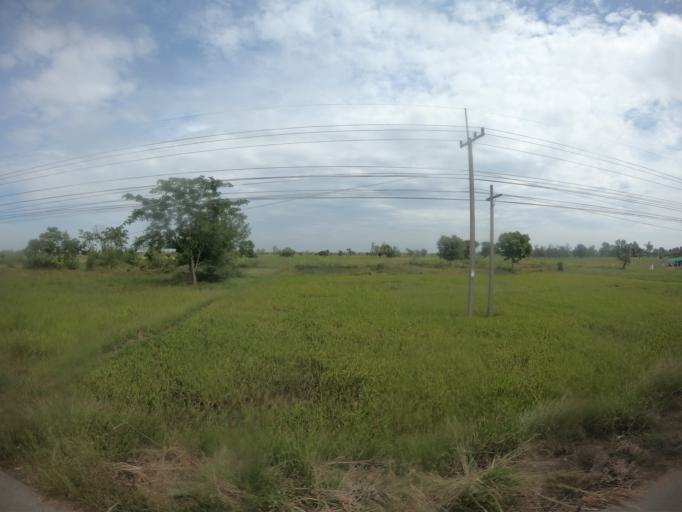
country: TH
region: Maha Sarakham
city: Chiang Yuen
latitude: 16.3564
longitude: 103.1145
